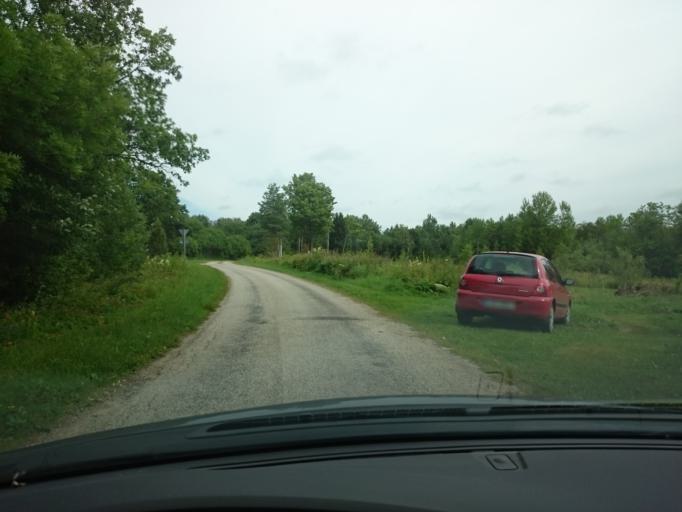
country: EE
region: Laeaene
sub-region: Ridala Parish
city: Uuemoisa
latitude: 58.9785
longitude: 23.6788
